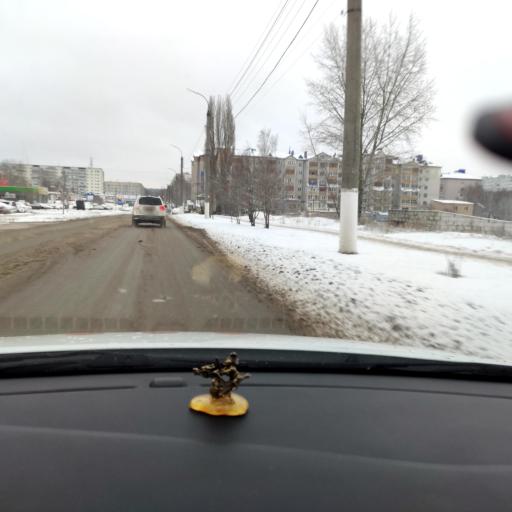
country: RU
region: Tatarstan
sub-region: Zelenodol'skiy Rayon
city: Zelenodolsk
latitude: 55.8596
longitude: 48.5558
